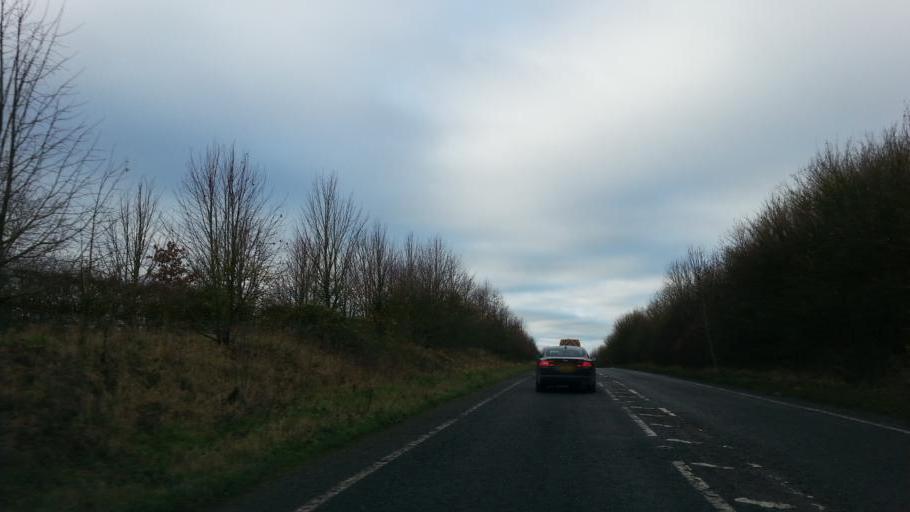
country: GB
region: England
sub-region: Suffolk
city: Botesdale
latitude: 52.3355
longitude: 0.9791
